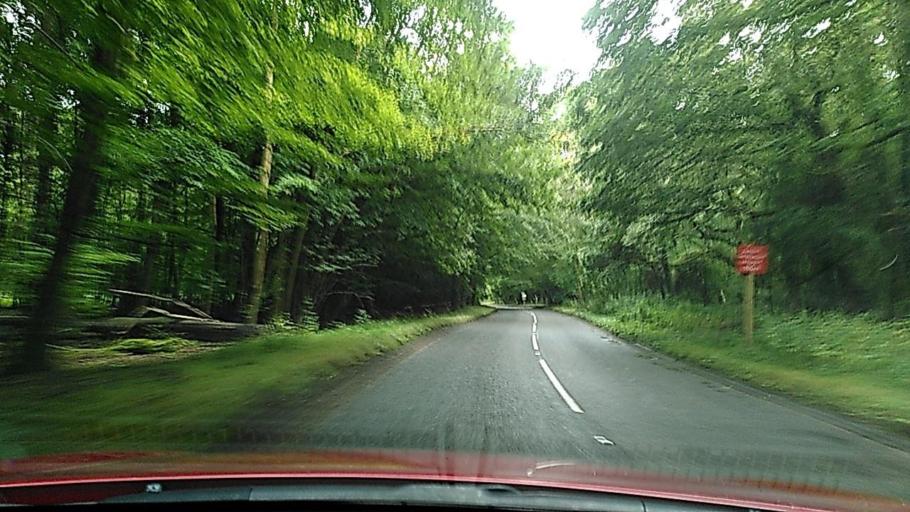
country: GB
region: England
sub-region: Oxfordshire
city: Rotherfield Peppard
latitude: 51.5650
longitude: -0.9878
